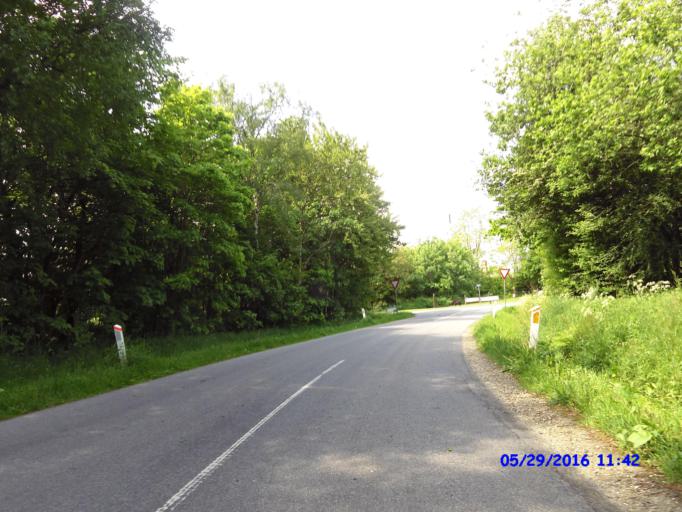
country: DK
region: South Denmark
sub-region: Haderslev Kommune
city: Gram
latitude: 55.3024
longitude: 9.0618
